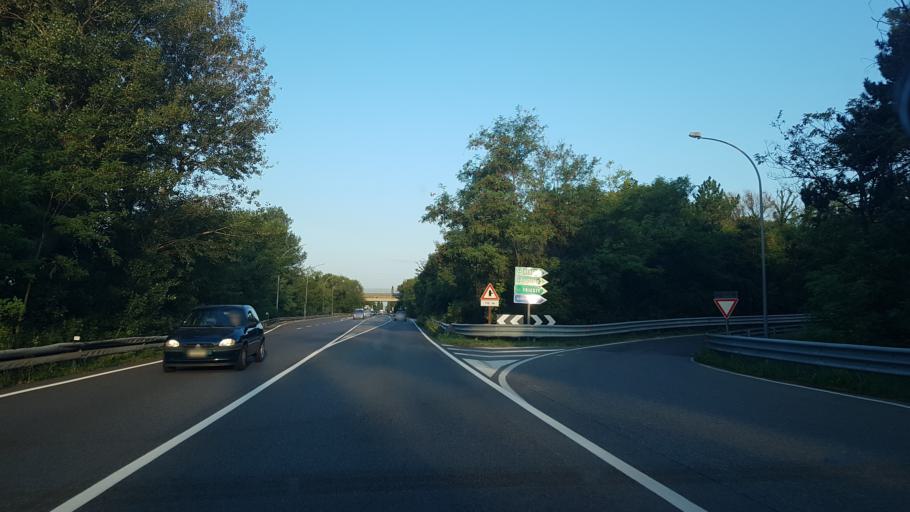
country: IT
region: Friuli Venezia Giulia
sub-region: Provincia di Gorizia
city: Monfalcone
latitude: 45.8006
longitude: 13.5711
